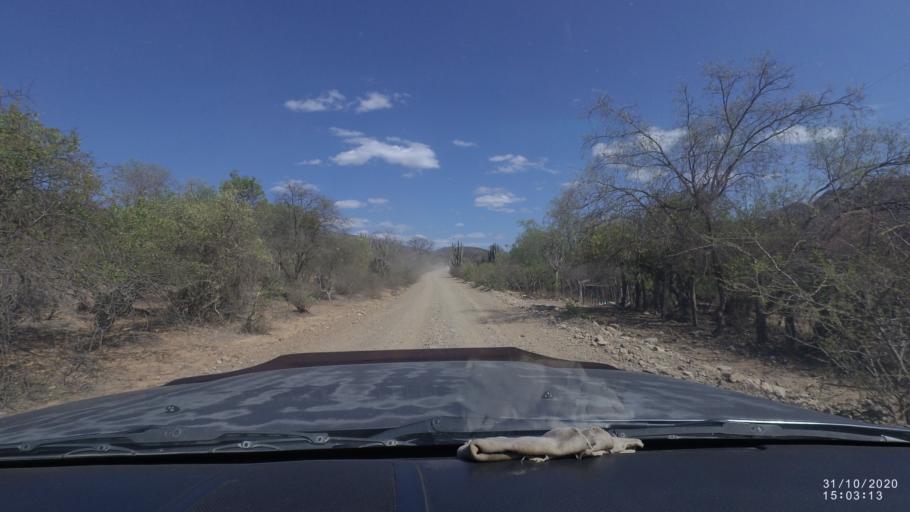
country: BO
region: Cochabamba
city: Aiquile
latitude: -18.2743
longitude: -64.8081
